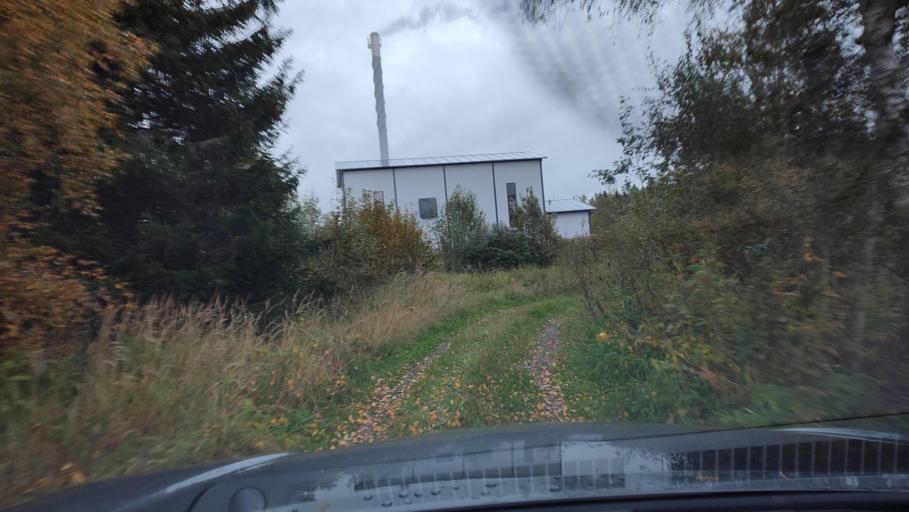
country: FI
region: Ostrobothnia
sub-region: Sydosterbotten
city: Kristinestad
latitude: 62.2781
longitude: 21.4073
